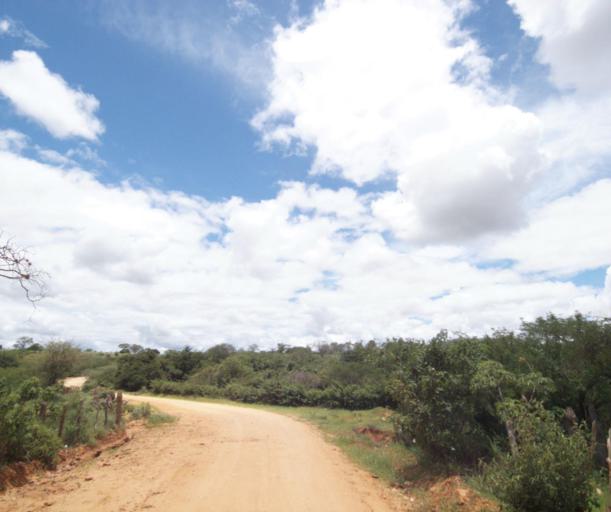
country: BR
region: Bahia
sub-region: Tanhacu
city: Tanhacu
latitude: -14.1595
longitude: -41.1789
